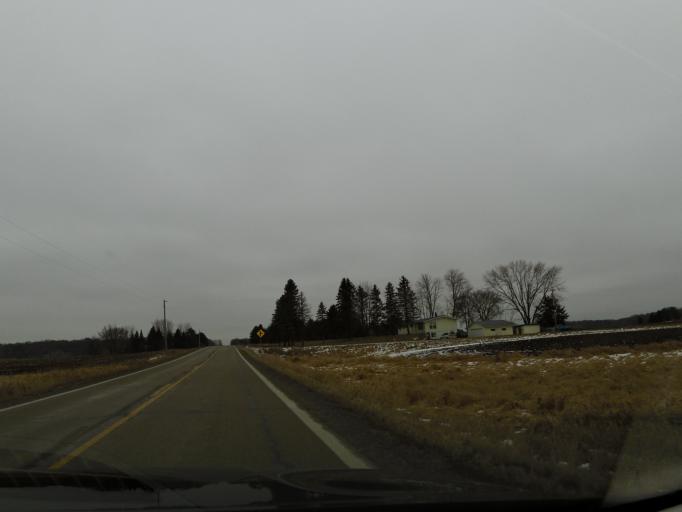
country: US
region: Minnesota
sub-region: Carver County
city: Watertown
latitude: 45.0062
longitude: -93.8489
